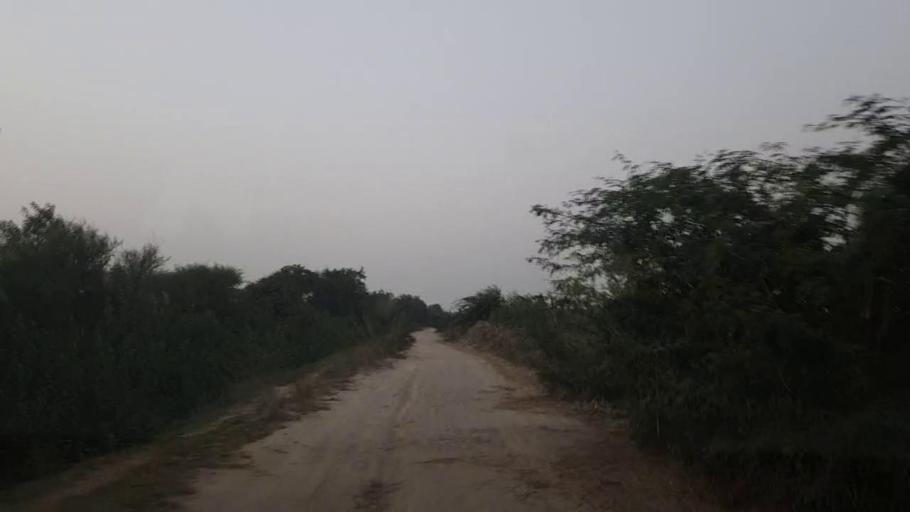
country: PK
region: Sindh
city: Mirpur Sakro
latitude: 24.5790
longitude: 67.7858
